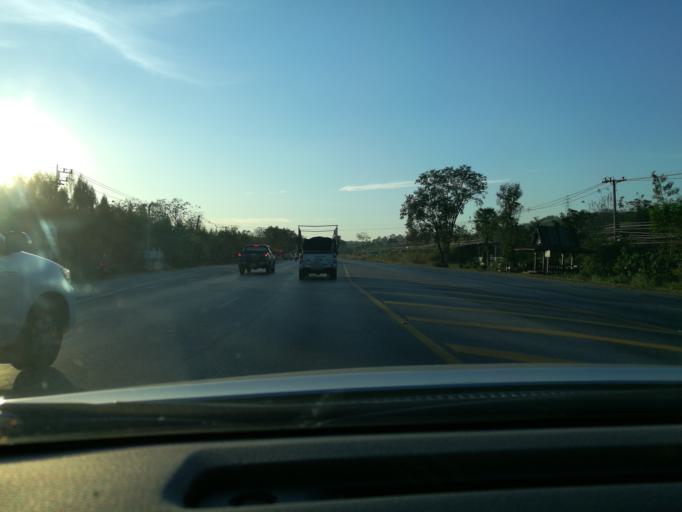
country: TH
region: Phitsanulok
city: Wang Thong
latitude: 16.8428
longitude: 100.5472
